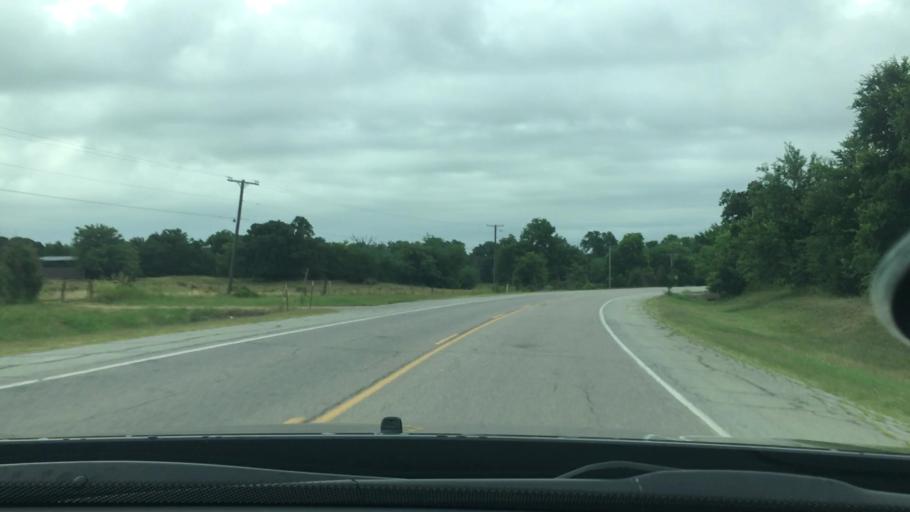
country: US
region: Oklahoma
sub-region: Coal County
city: Coalgate
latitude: 34.5488
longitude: -96.2315
